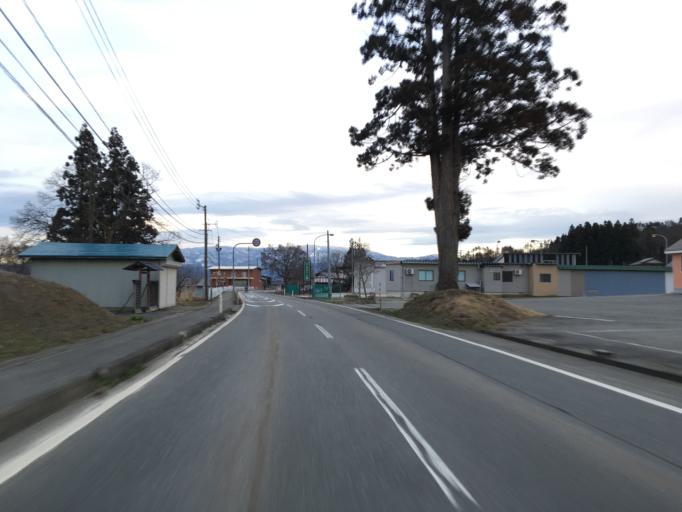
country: JP
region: Yamagata
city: Yonezawa
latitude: 37.9643
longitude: 140.0670
